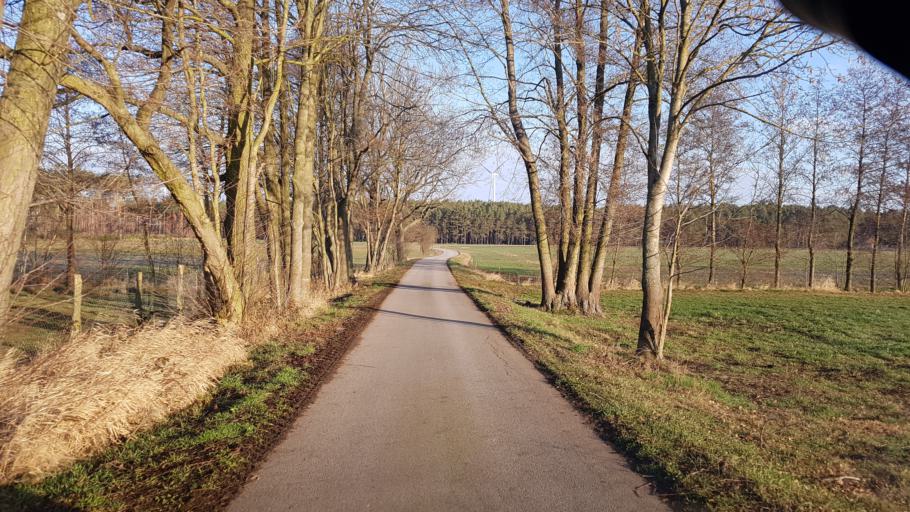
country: DE
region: Brandenburg
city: Calau
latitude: 51.7316
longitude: 13.8987
